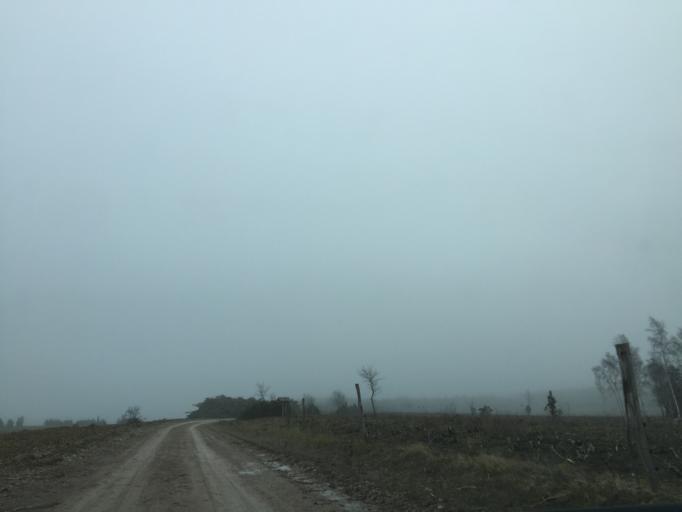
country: EE
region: Saare
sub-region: Kuressaare linn
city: Kuressaare
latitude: 58.5090
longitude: 21.9520
